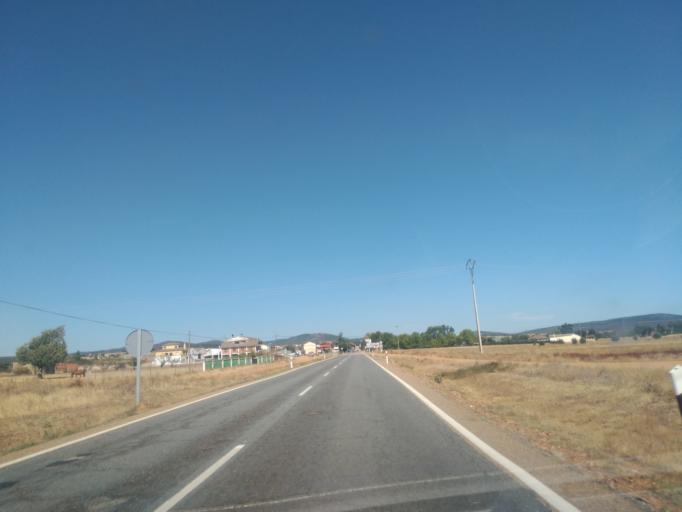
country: ES
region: Castille and Leon
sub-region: Provincia de Zamora
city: Tabara
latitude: 41.8188
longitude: -5.9467
